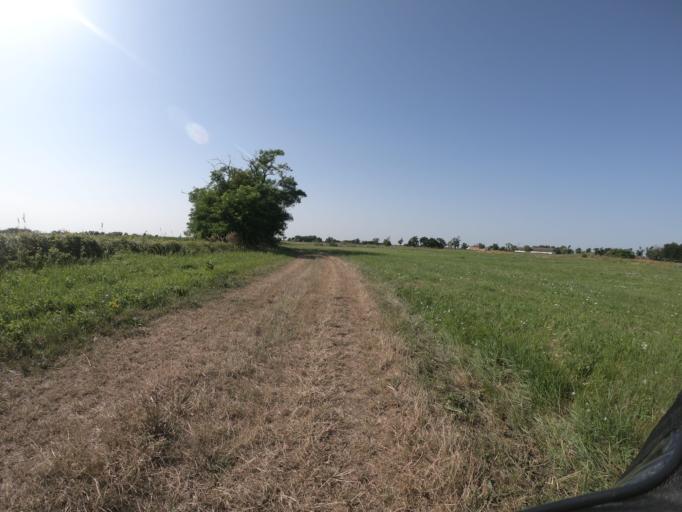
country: HU
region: Hajdu-Bihar
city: Egyek
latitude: 47.5753
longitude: 20.9463
